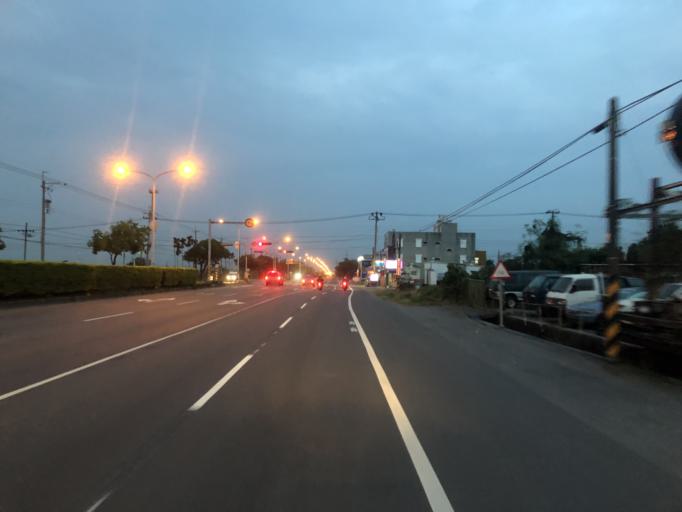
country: TW
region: Taiwan
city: Yujing
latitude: 23.1436
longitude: 120.3266
